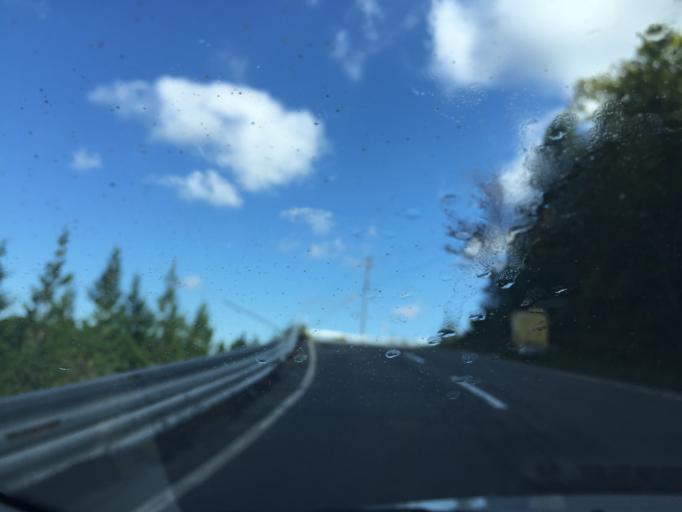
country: JP
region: Gifu
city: Nakatsugawa
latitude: 35.2979
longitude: 137.6723
